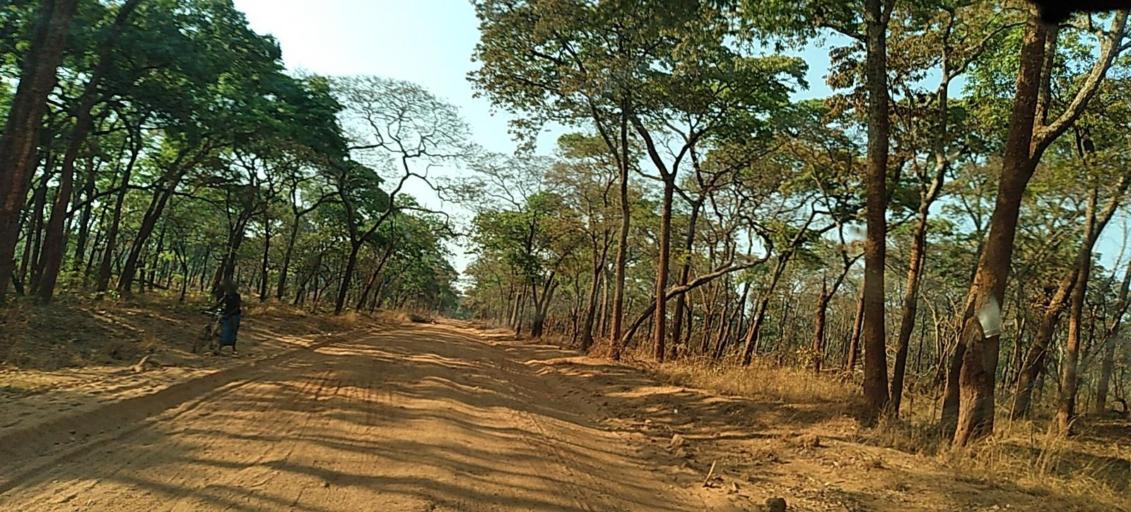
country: ZM
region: North-Western
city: Kasempa
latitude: -13.5540
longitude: 25.9981
